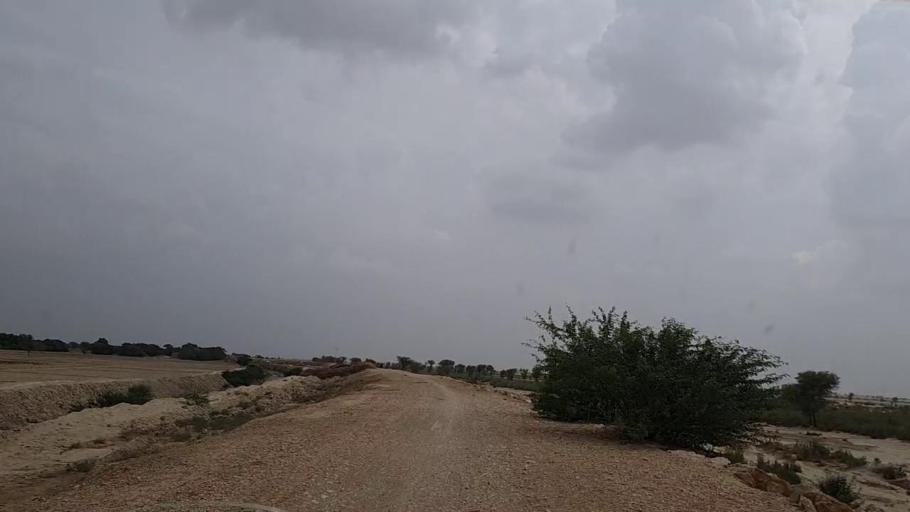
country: PK
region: Sindh
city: Johi
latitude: 26.7262
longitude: 67.5780
